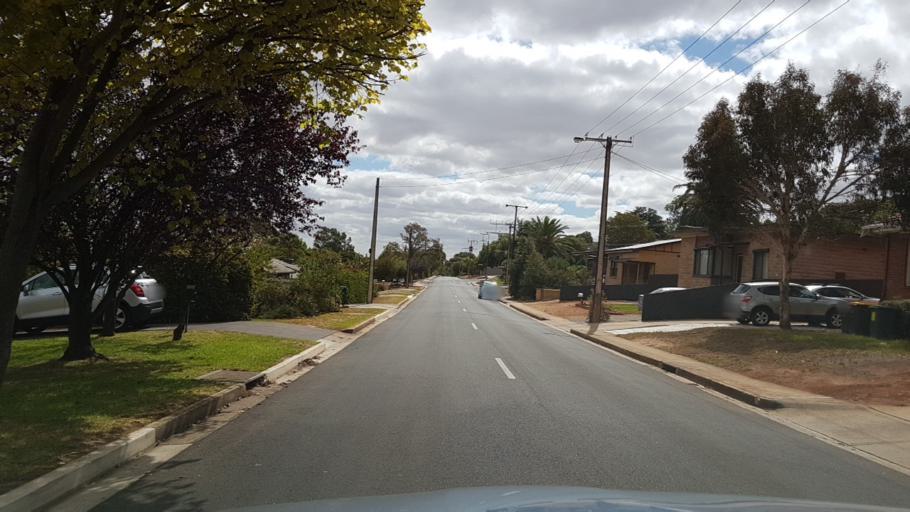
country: AU
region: South Australia
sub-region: Gawler
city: Gawler
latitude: -34.6082
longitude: 138.7532
